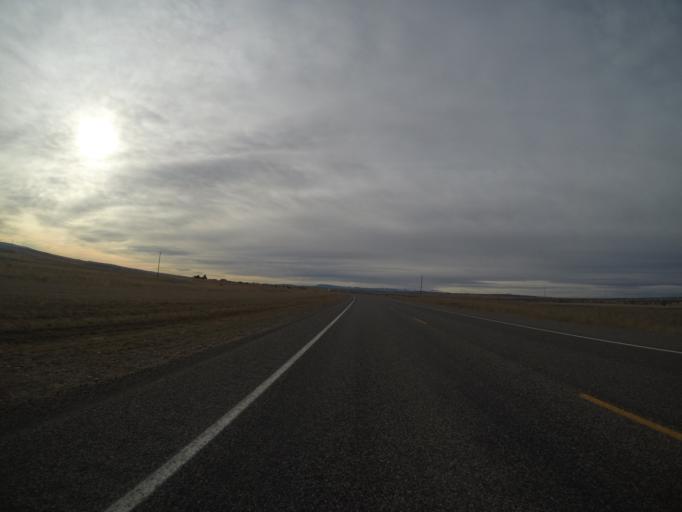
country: US
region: Montana
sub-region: Yellowstone County
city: Laurel
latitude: 45.5881
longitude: -108.8366
